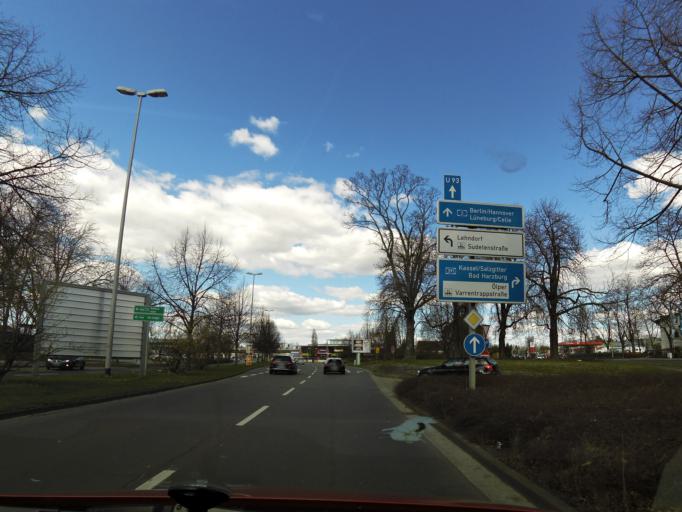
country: DE
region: Lower Saxony
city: Braunschweig
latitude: 52.2783
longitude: 10.5047
